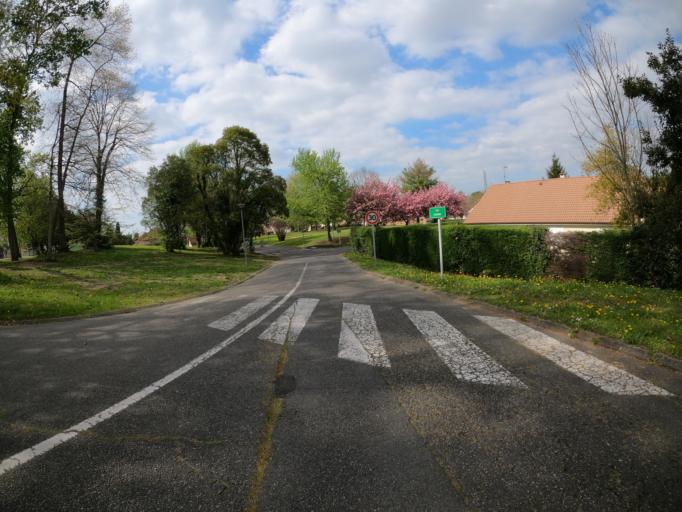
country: FR
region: Aquitaine
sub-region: Departement des Pyrenees-Atlantiques
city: Lons
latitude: 43.3268
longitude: -0.3890
